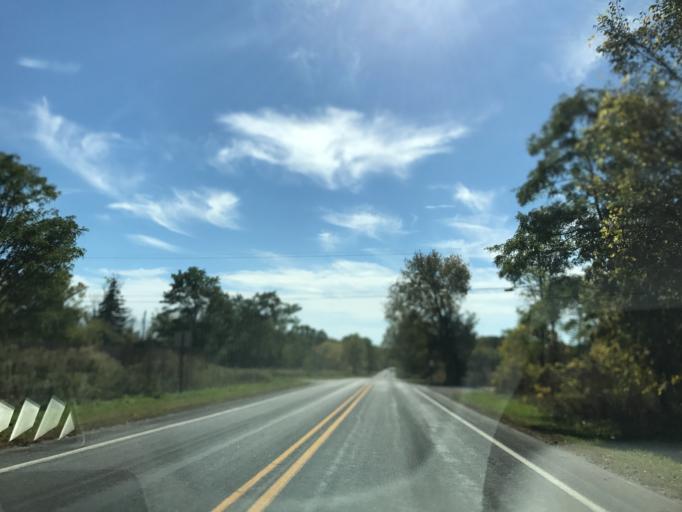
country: US
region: Michigan
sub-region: Washtenaw County
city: Ann Arbor
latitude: 42.3470
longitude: -83.6621
